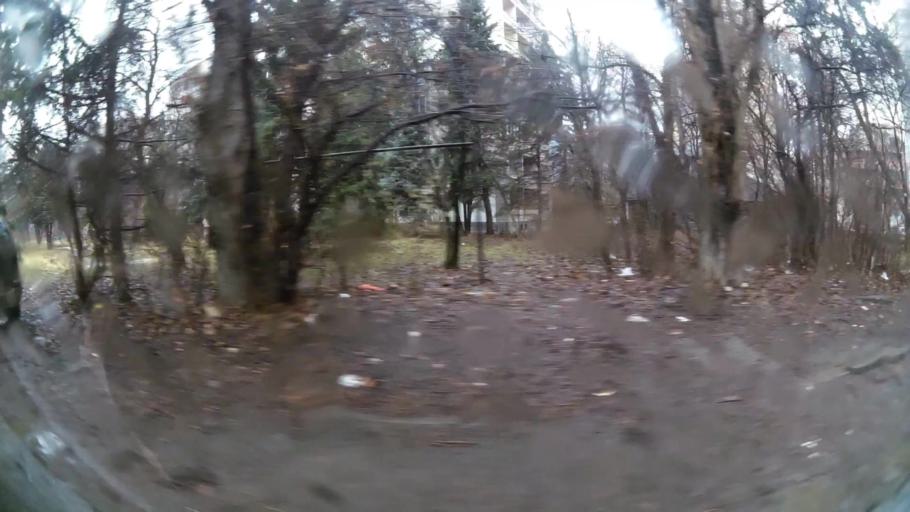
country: BG
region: Sofia-Capital
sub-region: Stolichna Obshtina
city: Sofia
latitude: 42.6570
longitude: 23.3811
